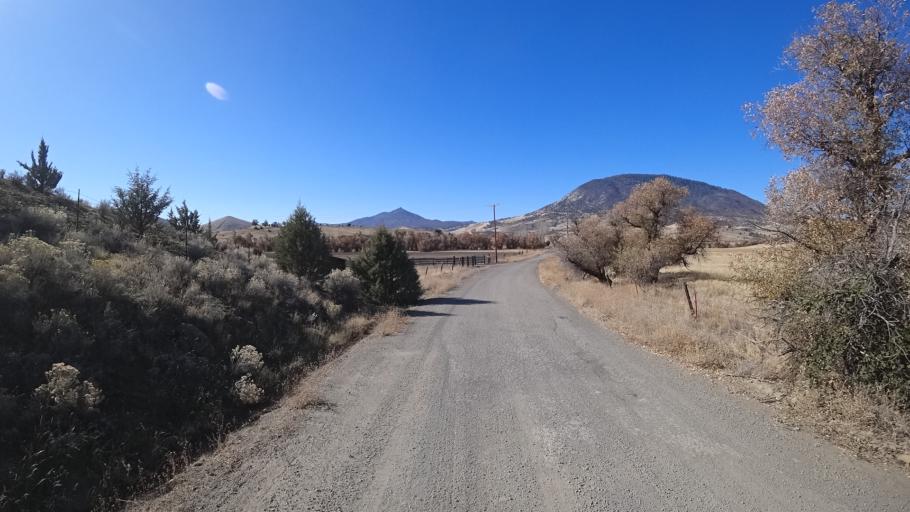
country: US
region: California
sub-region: Siskiyou County
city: Montague
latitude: 41.8480
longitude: -122.4524
